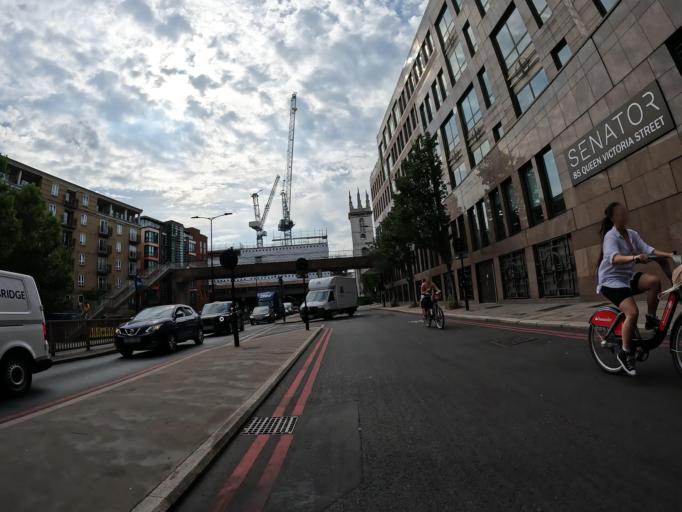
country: GB
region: England
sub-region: Greater London
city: Bethnal Green
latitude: 51.5350
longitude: -0.0774
